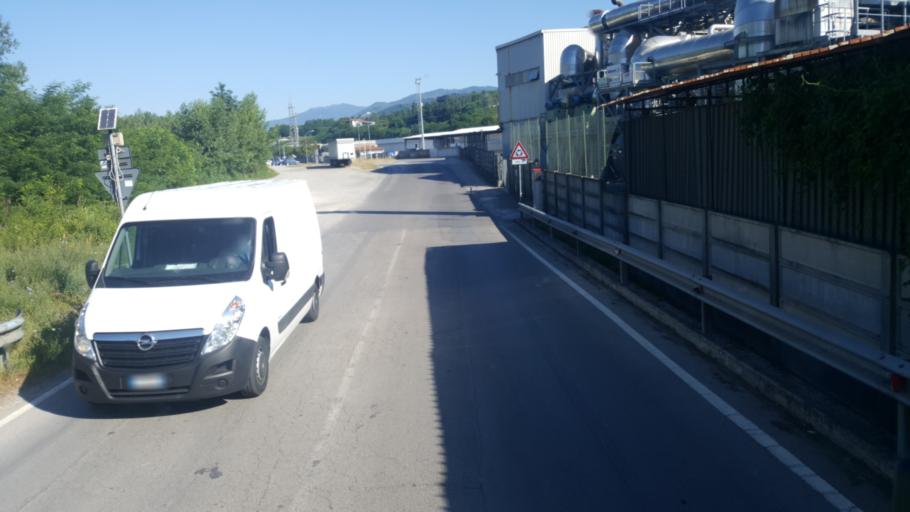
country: IT
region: Tuscany
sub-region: Provincia di Lucca
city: Castelnuovo di Garfagnana
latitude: 44.1178
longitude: 10.4036
